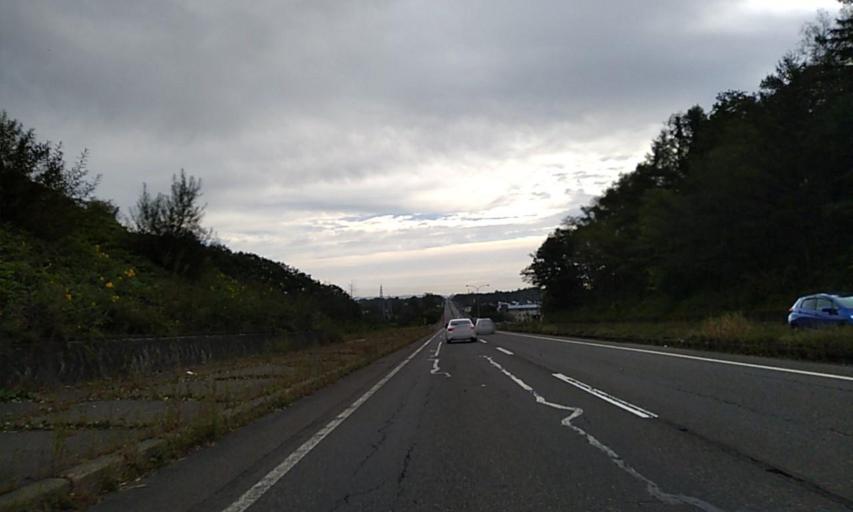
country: JP
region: Hokkaido
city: Obihiro
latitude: 42.9193
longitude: 143.0263
